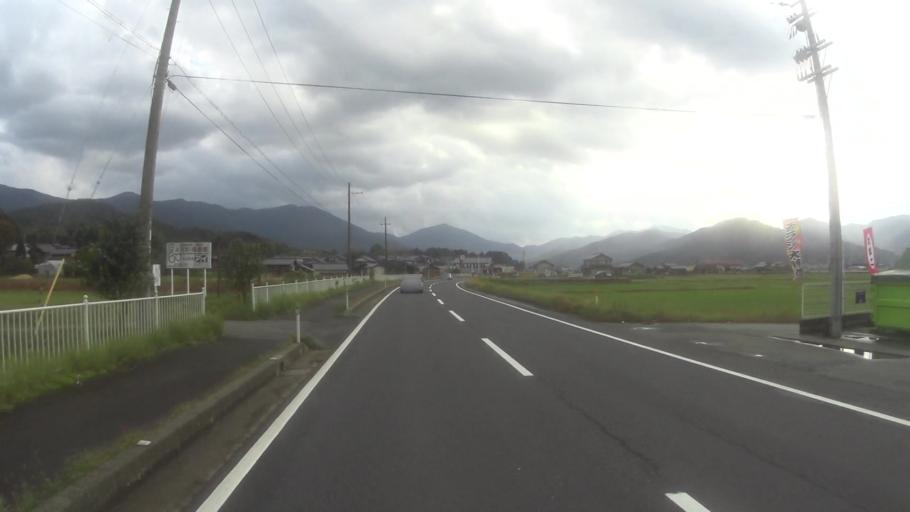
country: JP
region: Kyoto
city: Miyazu
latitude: 35.5142
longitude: 135.1070
